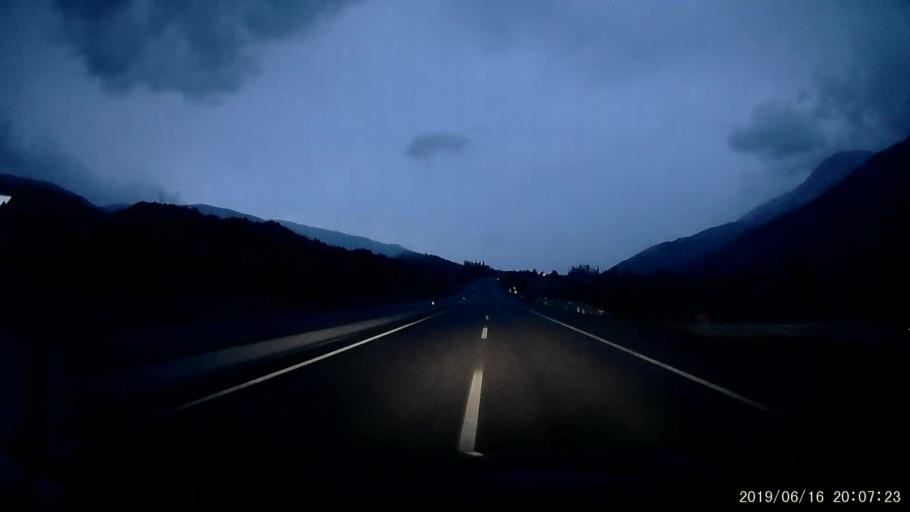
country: TR
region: Sivas
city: Dogansar
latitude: 40.3183
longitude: 37.6252
